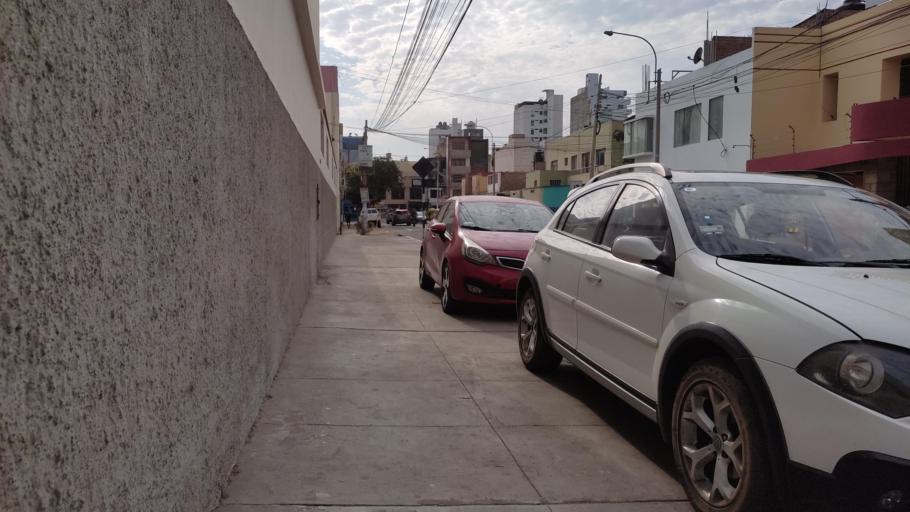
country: PE
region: La Libertad
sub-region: Provincia de Trujillo
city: Trujillo
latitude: -8.1182
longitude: -79.0343
